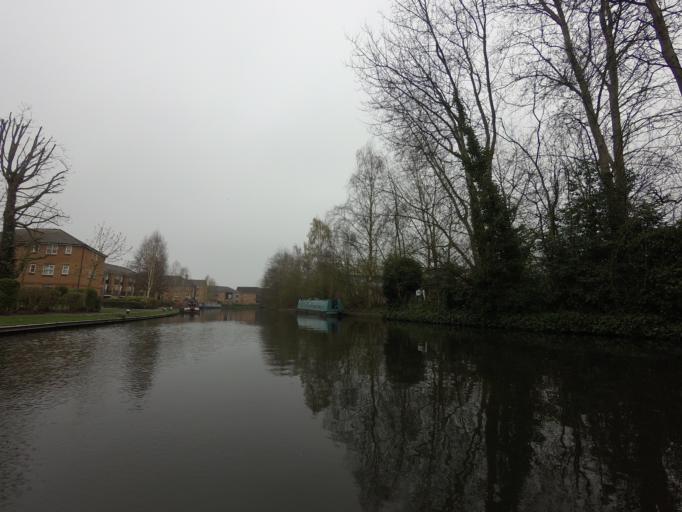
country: GB
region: England
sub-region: Hertfordshire
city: Hemel Hempstead
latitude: 51.7361
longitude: -0.4634
